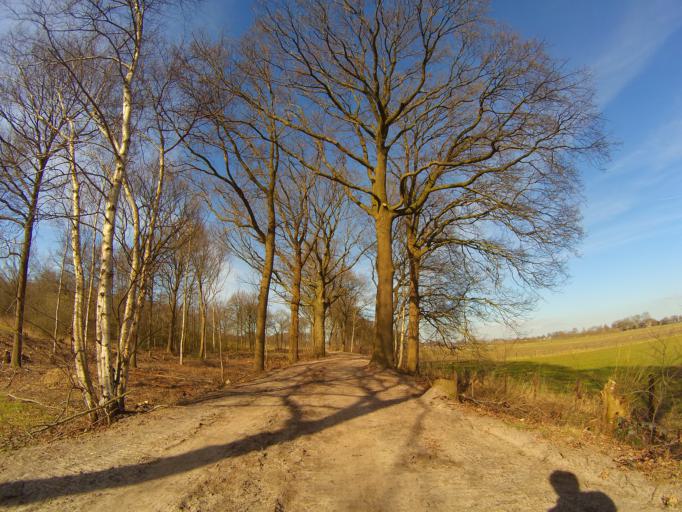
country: NL
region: Gelderland
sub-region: Gemeente Ede
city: Ederveen
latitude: 52.0804
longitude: 5.5611
